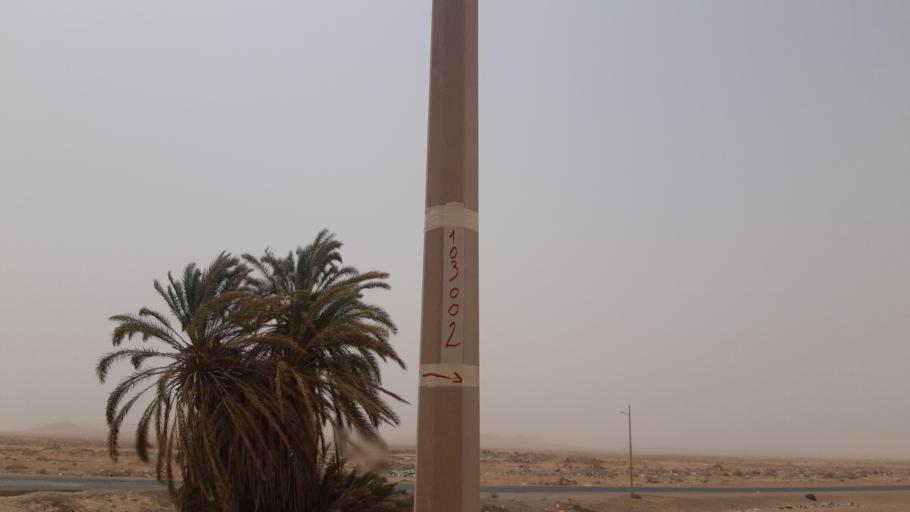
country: TN
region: Qibili
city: Kebili
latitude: 33.7810
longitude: 9.0058
